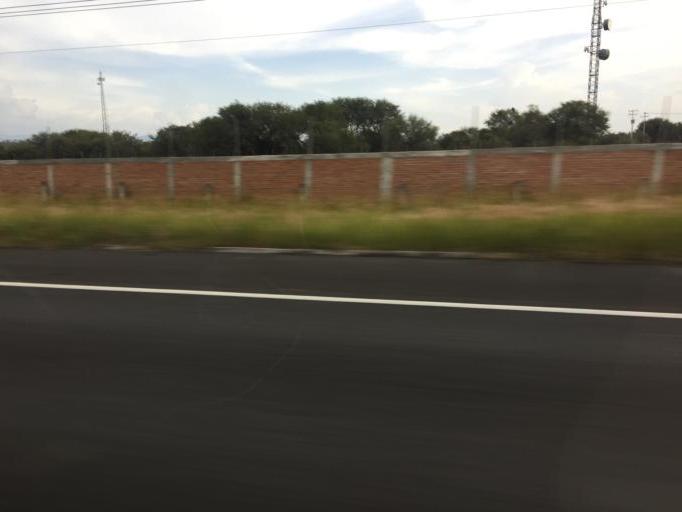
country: MX
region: Michoacan
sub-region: Alvaro Obregon
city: Tzintzimeo
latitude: 19.8910
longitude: -100.9823
